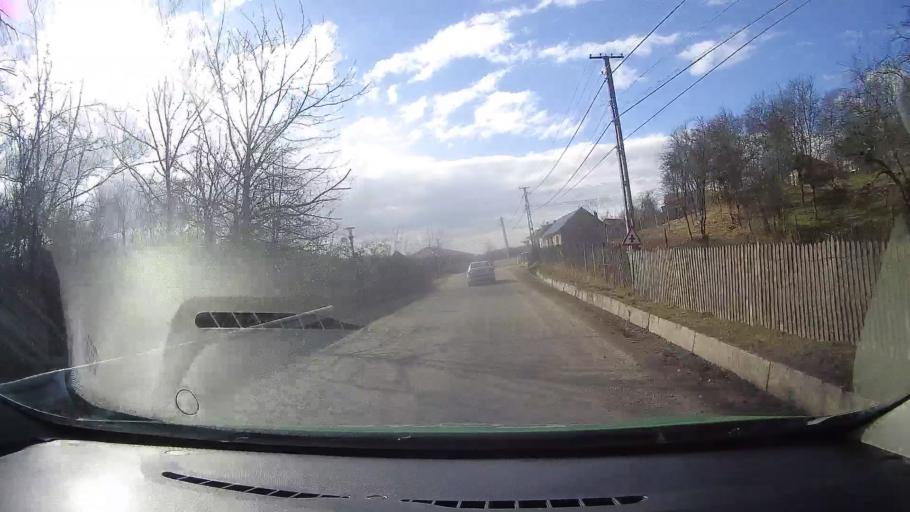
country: RO
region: Dambovita
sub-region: Comuna Varfuri
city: Varfuri
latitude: 45.0955
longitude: 25.5079
